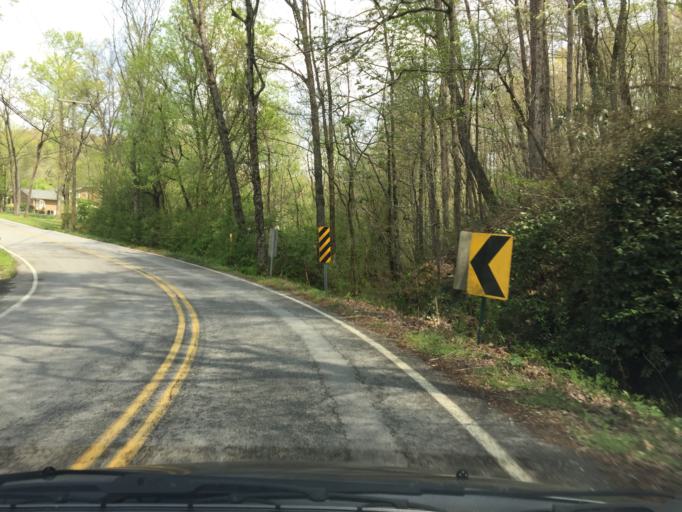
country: US
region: Tennessee
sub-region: Hamilton County
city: Walden
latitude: 35.1567
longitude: -85.2801
